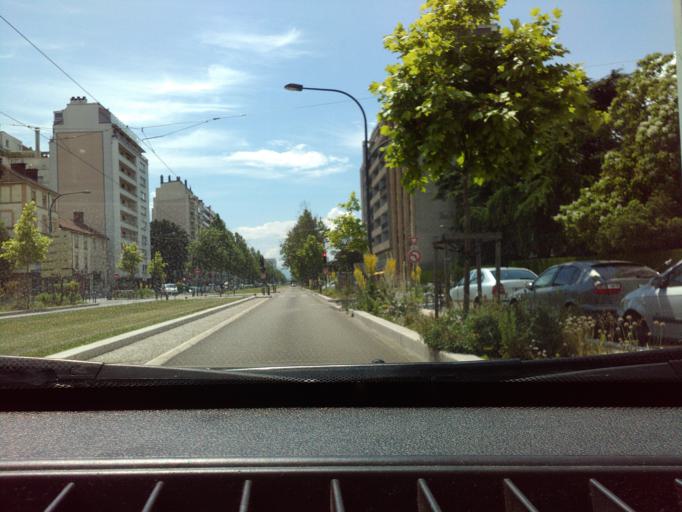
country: FR
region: Rhone-Alpes
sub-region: Departement de l'Isere
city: Grenoble
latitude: 45.1782
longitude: 5.7156
